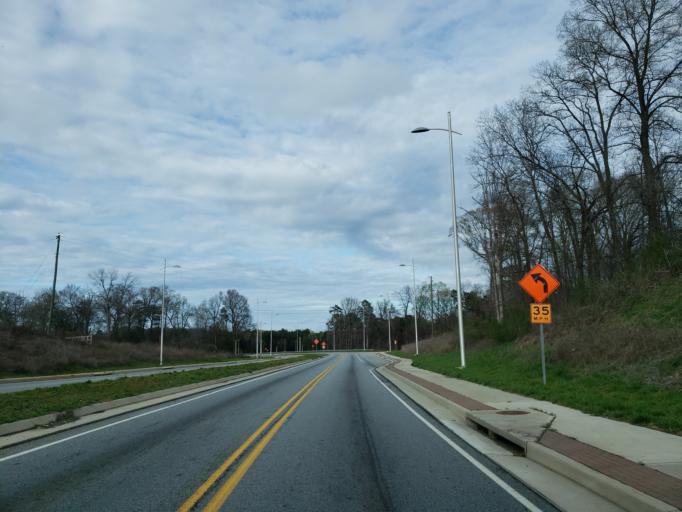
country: US
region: Georgia
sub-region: Clayton County
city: Forest Park
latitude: 33.6365
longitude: -84.3895
